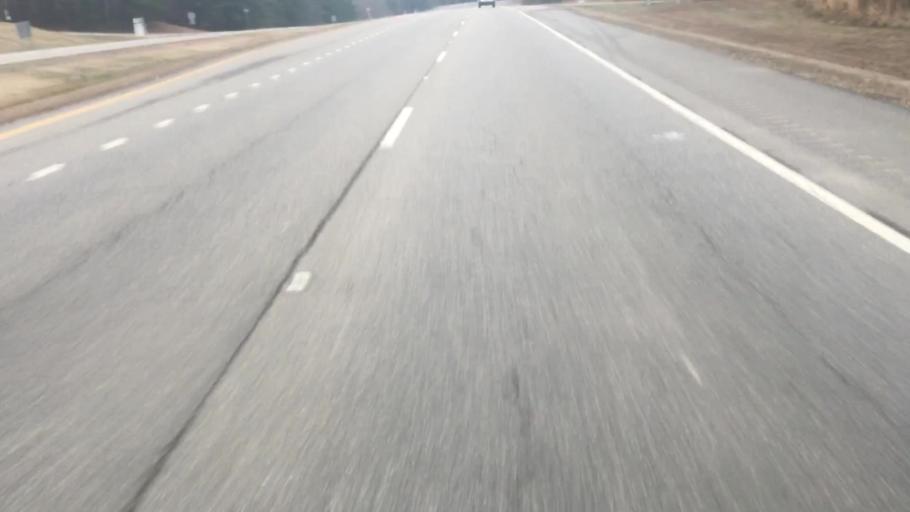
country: US
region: Alabama
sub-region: Walker County
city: Sumiton
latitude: 33.7390
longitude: -87.0293
